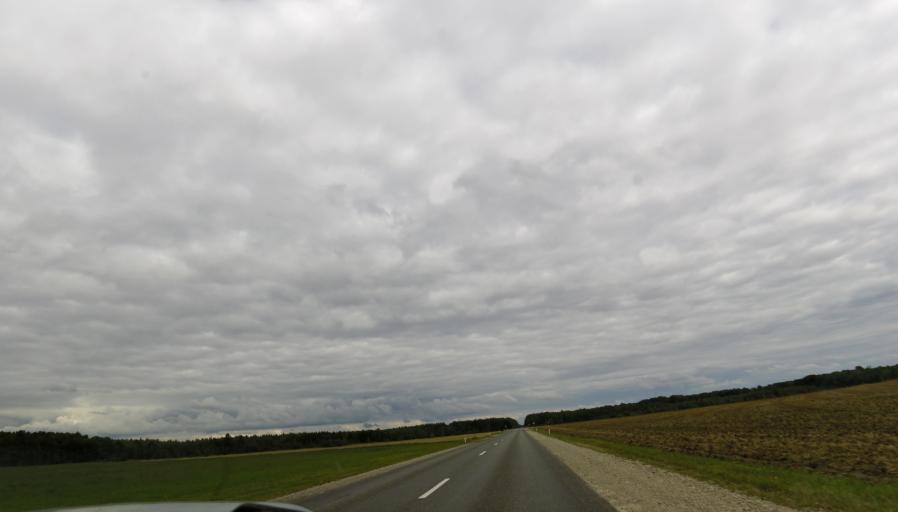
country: LT
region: Panevezys
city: Pasvalys
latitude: 56.0290
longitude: 24.2594
